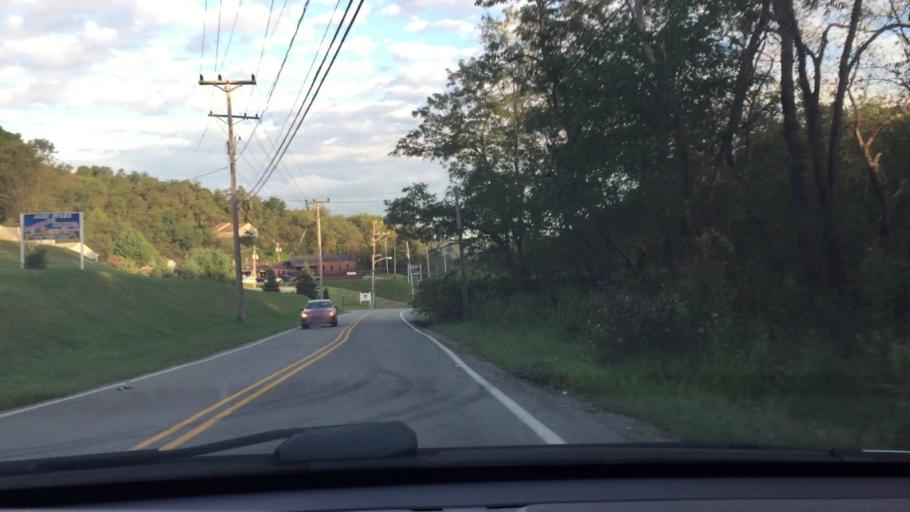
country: US
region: Pennsylvania
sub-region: Westmoreland County
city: Murrysville
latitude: 40.4529
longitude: -79.7301
